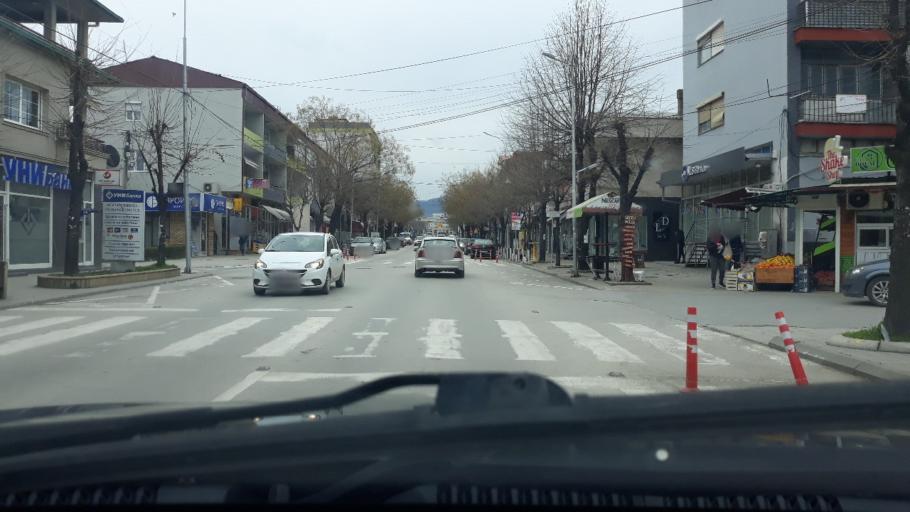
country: MK
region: Kavadarci
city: Kavadarci
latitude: 41.4365
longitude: 22.0110
